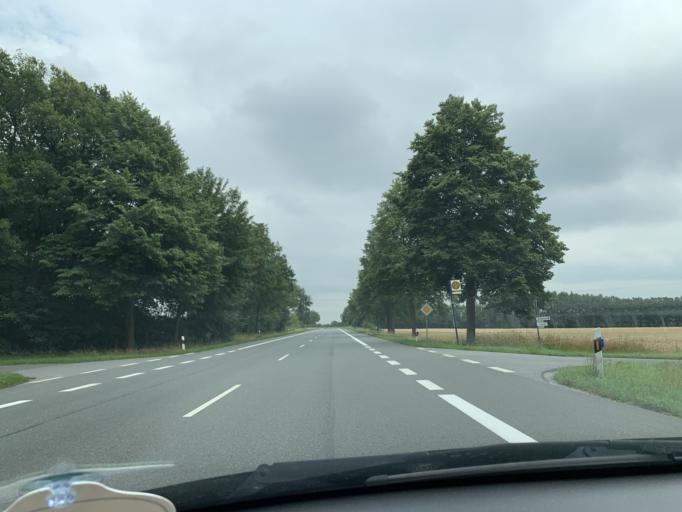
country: DE
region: North Rhine-Westphalia
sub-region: Regierungsbezirk Munster
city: Warendorf
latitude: 51.9350
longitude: 8.0205
